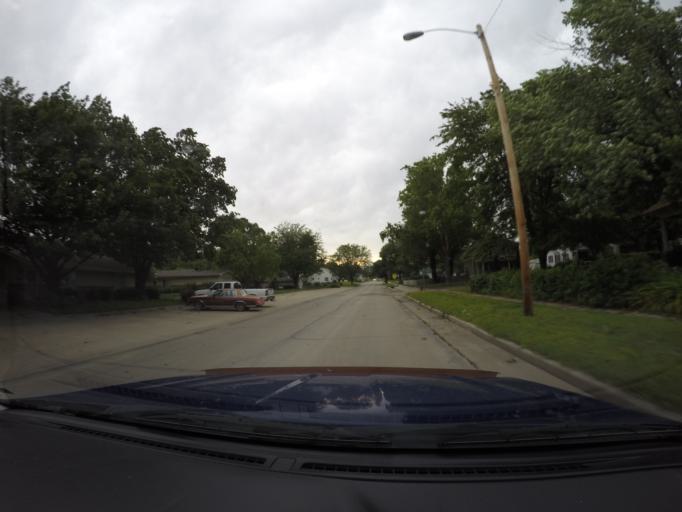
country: US
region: Kansas
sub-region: Clay County
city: Clay Center
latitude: 39.3789
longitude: -97.1192
